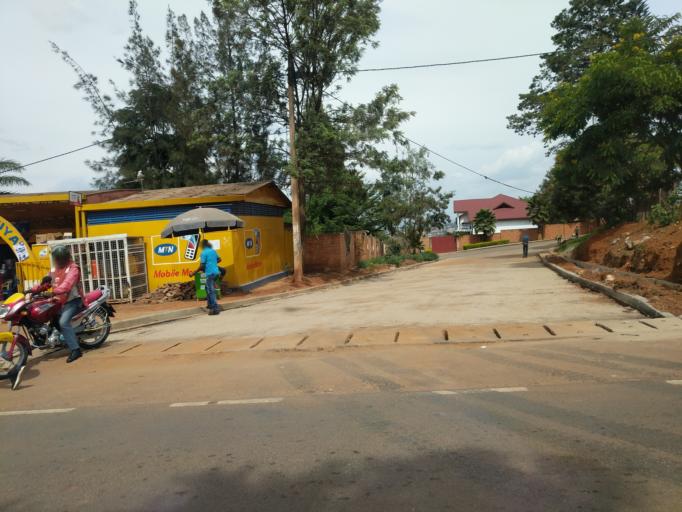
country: RW
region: Kigali
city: Kigali
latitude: -1.9715
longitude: 30.1035
